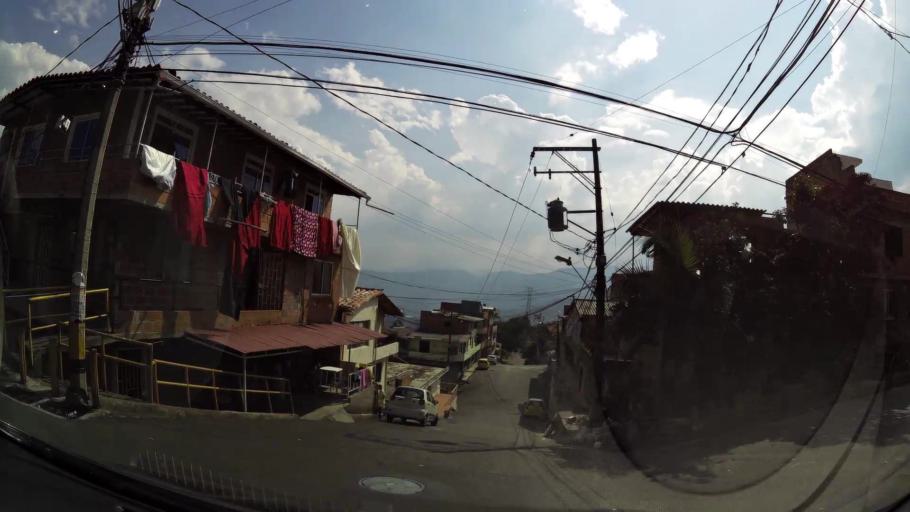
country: CO
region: Antioquia
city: Medellin
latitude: 6.2883
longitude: -75.5942
